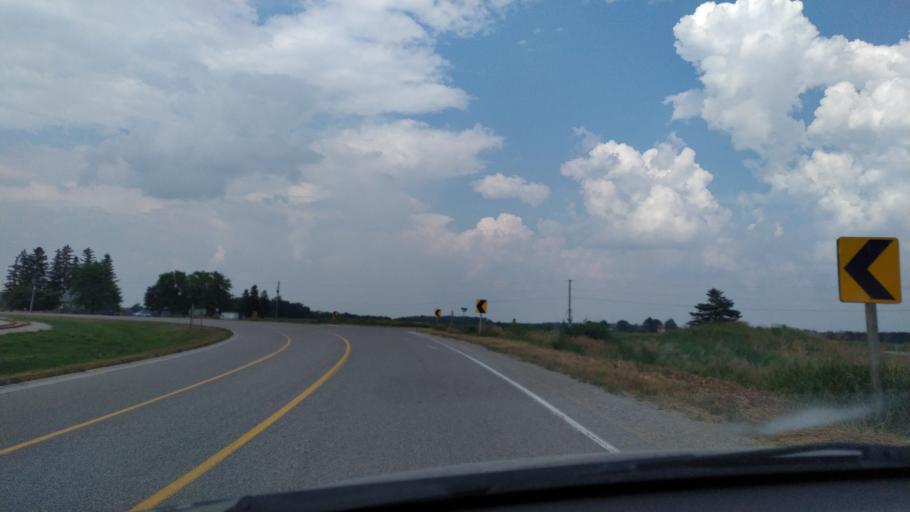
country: CA
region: Ontario
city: Dorchester
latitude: 43.1669
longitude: -81.1372
